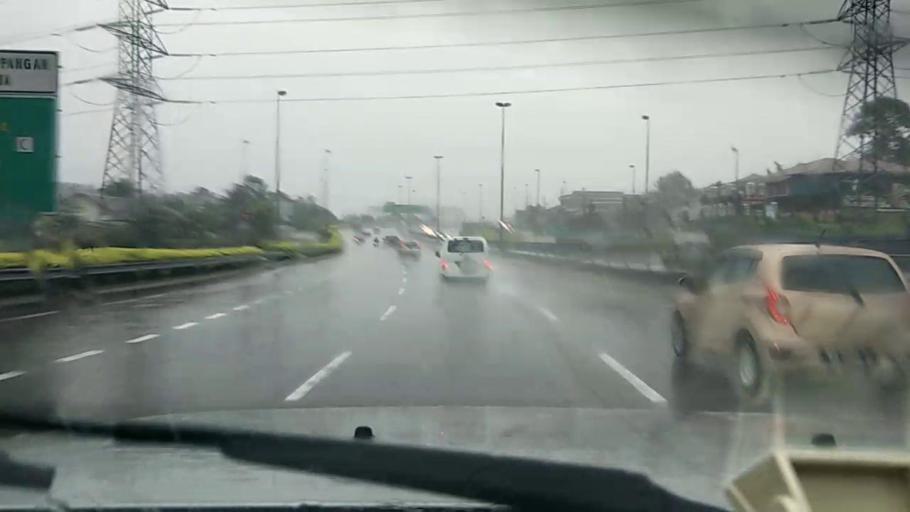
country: MY
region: Selangor
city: Kampong Baharu Balakong
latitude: 2.9876
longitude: 101.7676
